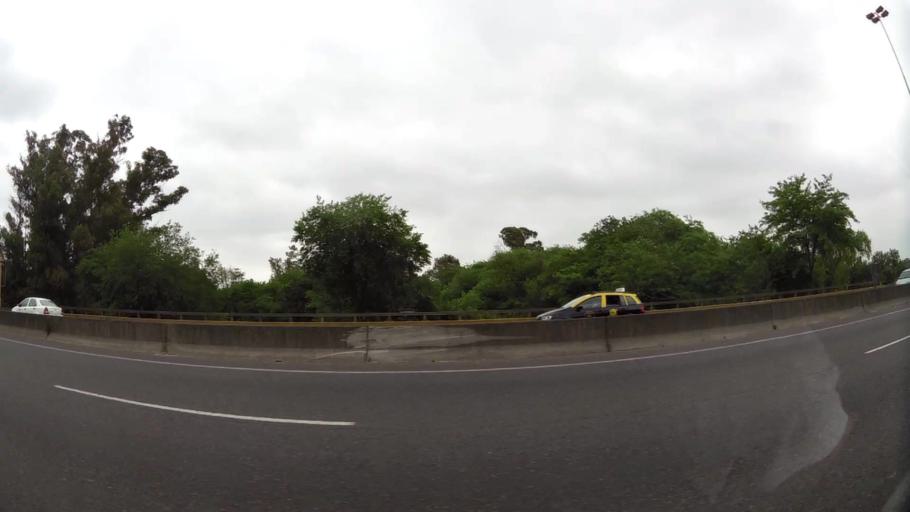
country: AR
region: Buenos Aires
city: San Justo
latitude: -34.7407
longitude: -58.5204
